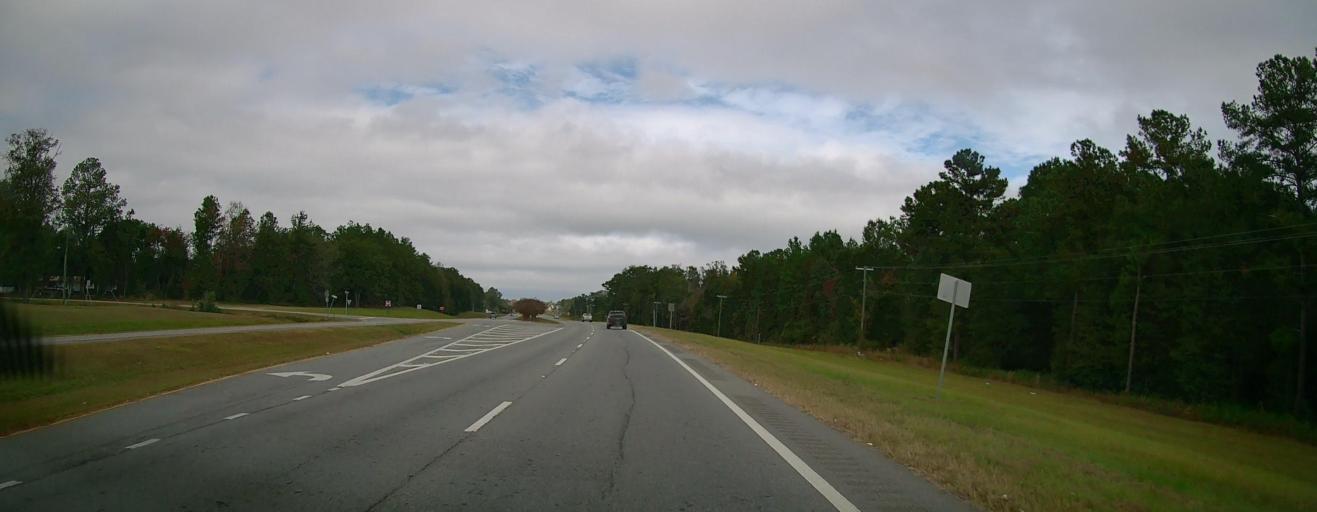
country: US
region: Georgia
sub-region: Colquitt County
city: Moultrie
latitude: 31.1546
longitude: -83.7618
